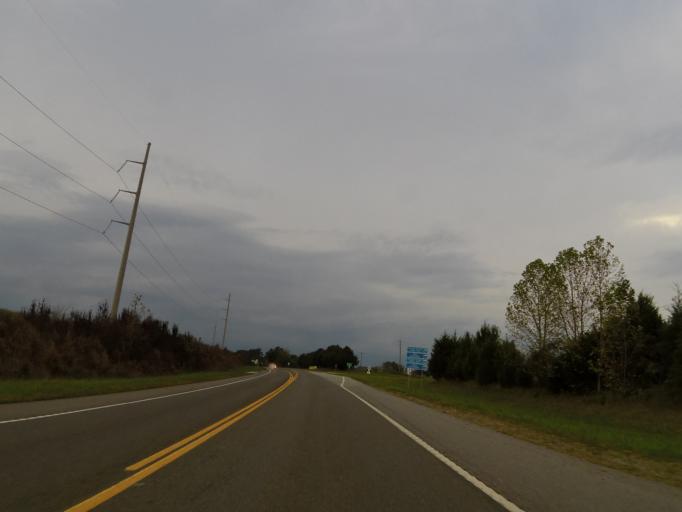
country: US
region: Tennessee
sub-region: Monroe County
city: Vonore
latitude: 35.6589
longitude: -84.2880
